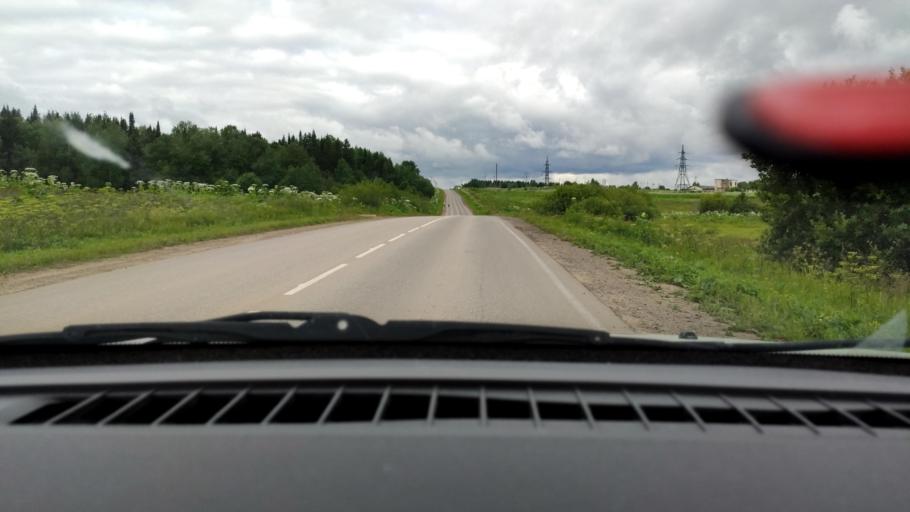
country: RU
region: Perm
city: Chaykovskaya
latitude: 58.1217
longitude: 55.5636
